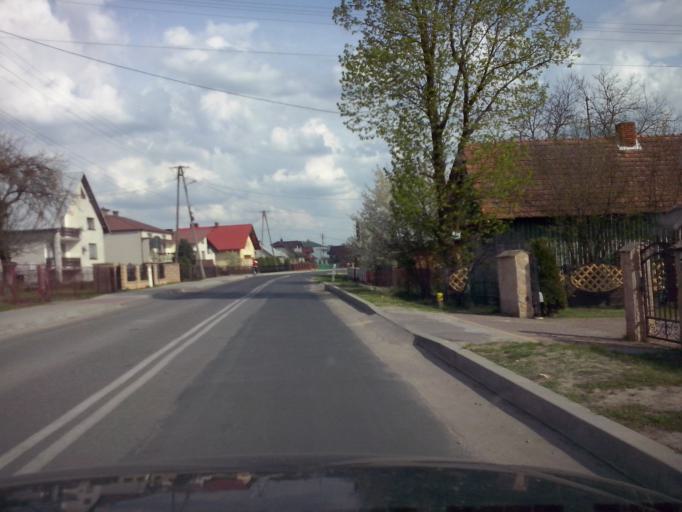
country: PL
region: Subcarpathian Voivodeship
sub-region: Powiat lezajski
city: Letownia
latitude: 50.3672
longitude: 22.2192
